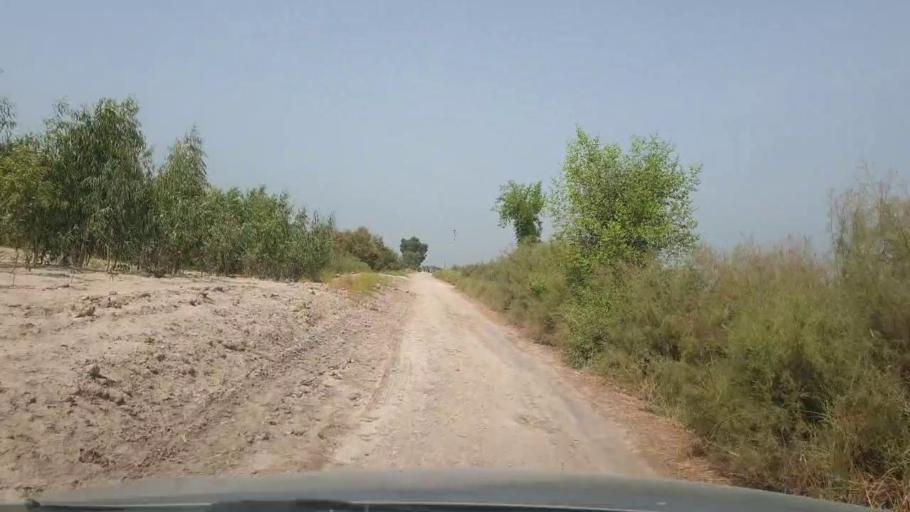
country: PK
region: Sindh
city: Garhi Yasin
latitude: 27.9098
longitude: 68.3985
